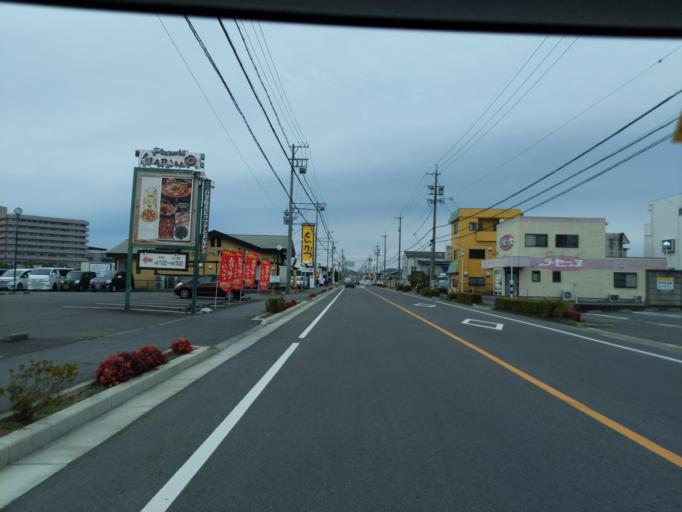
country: JP
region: Aichi
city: Kasugai
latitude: 35.2684
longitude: 136.9720
